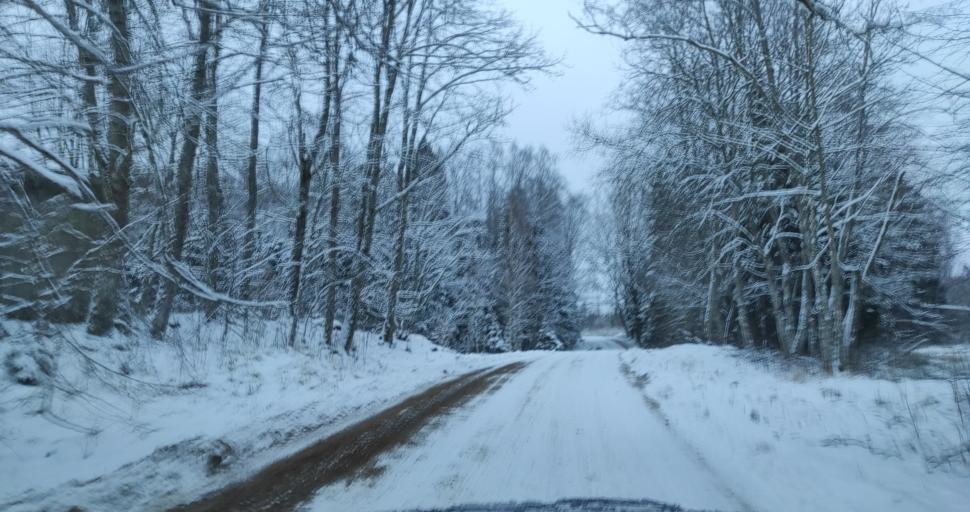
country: LV
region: Alsunga
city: Alsunga
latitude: 56.9579
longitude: 21.7146
